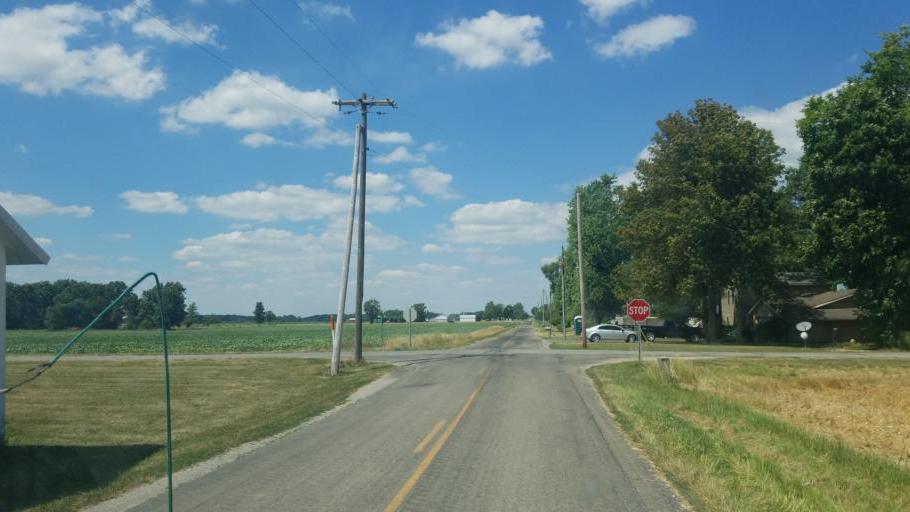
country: US
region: Ohio
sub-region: Defiance County
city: Hicksville
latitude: 41.3101
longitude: -84.7282
